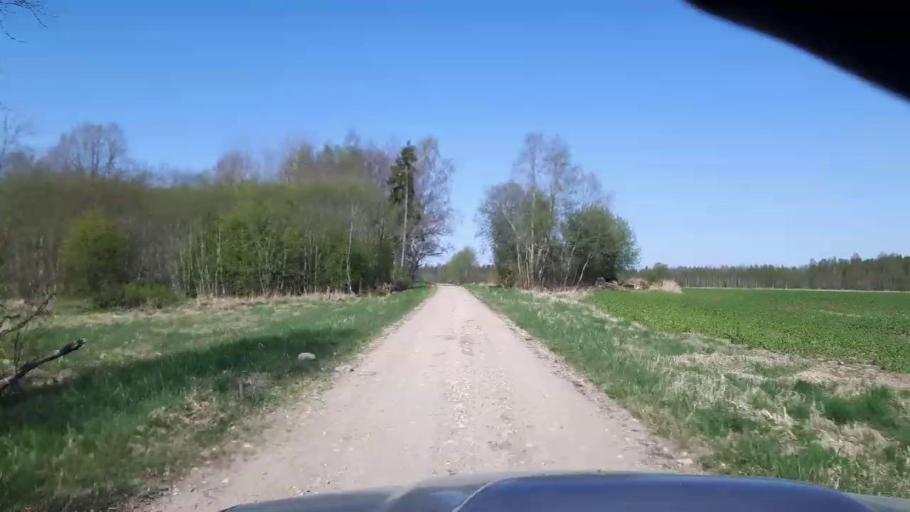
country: EE
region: Paernumaa
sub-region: Tootsi vald
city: Tootsi
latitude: 58.4460
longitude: 24.8048
